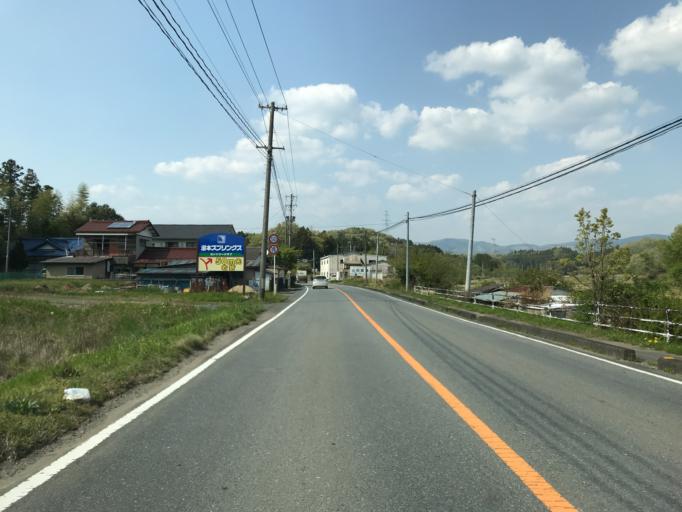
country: JP
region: Fukushima
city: Iwaki
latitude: 36.9595
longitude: 140.7543
